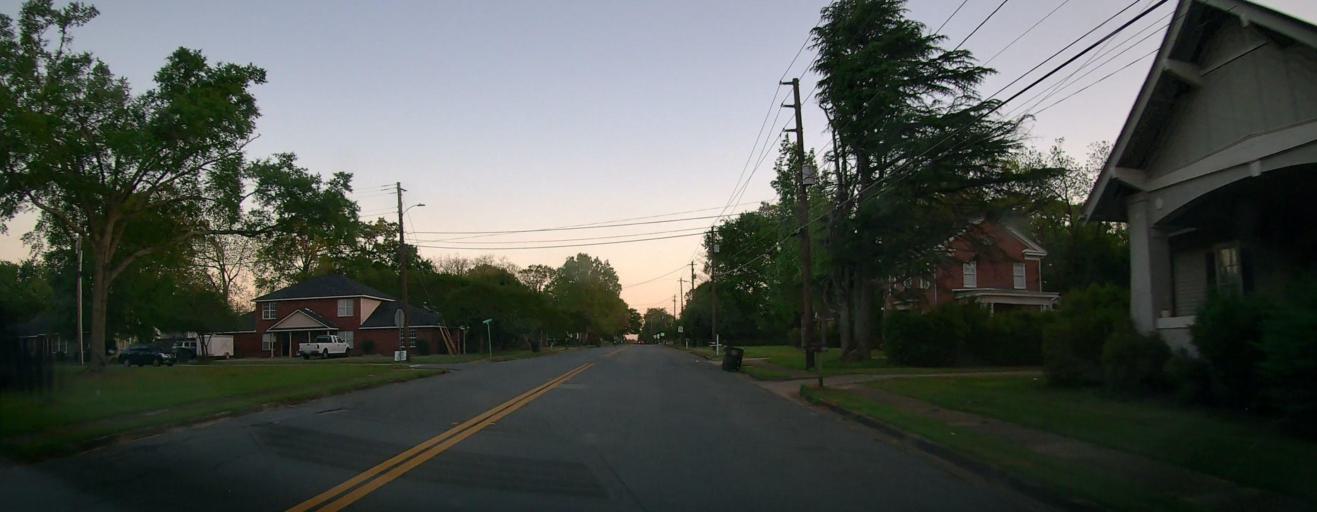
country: US
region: Georgia
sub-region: Marion County
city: Buena Vista
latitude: 32.3233
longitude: -84.5198
